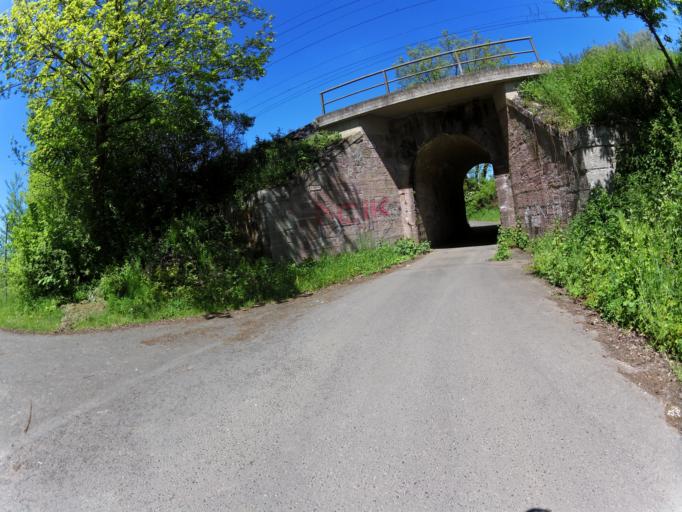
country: DE
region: Thuringia
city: Dankmarshausen
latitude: 50.9513
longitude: 10.0165
